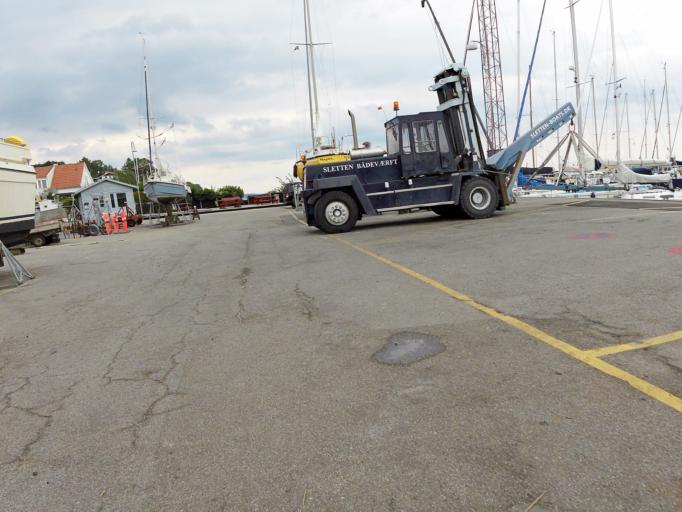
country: DK
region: Capital Region
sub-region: Fredensborg Kommune
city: Humlebaek
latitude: 55.9536
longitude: 12.5353
